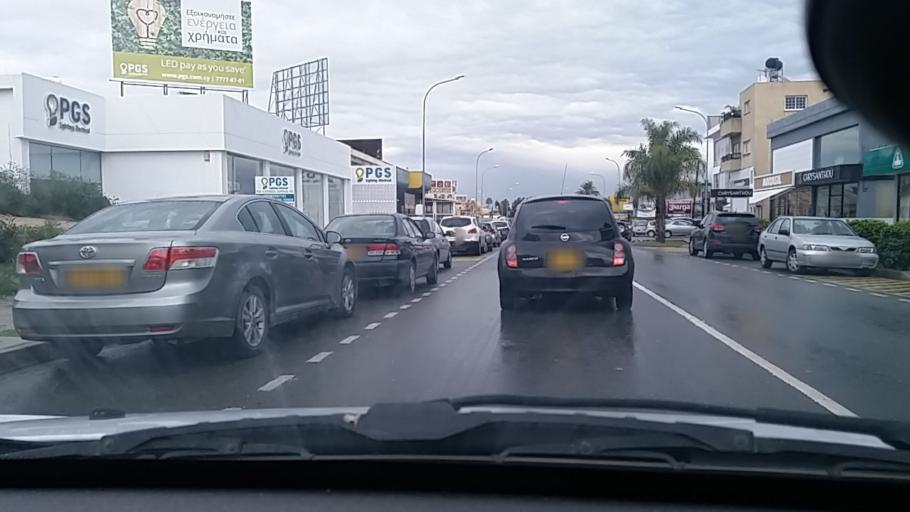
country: CY
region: Larnaka
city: Larnaca
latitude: 34.9281
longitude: 33.6170
